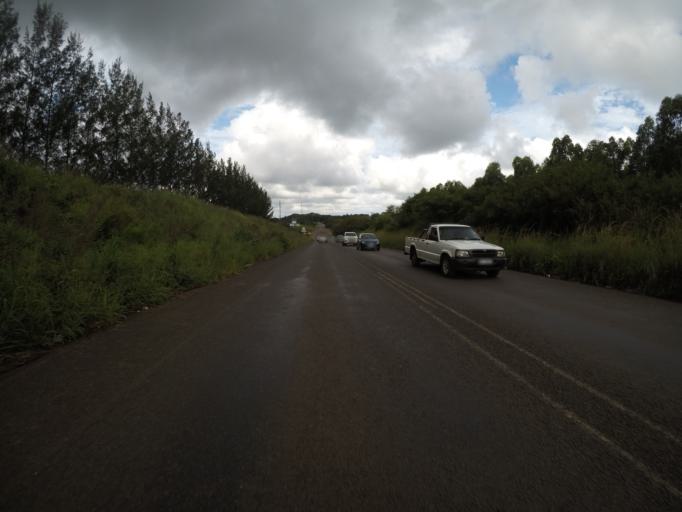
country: ZA
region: KwaZulu-Natal
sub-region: uMkhanyakude District Municipality
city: Mtubatuba
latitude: -28.4179
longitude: 32.1772
